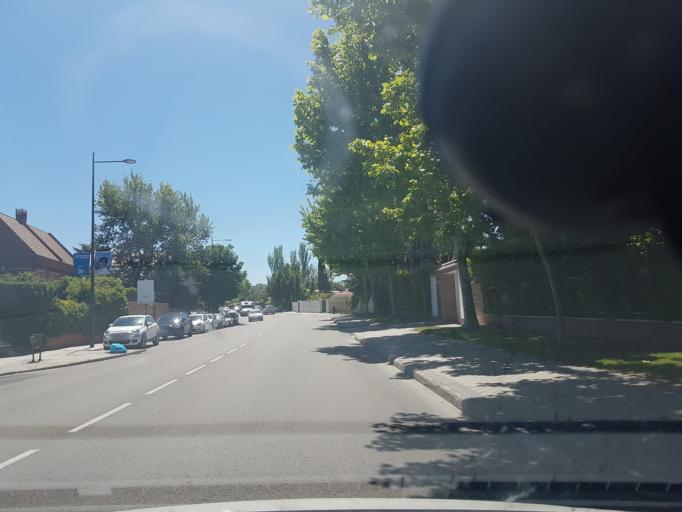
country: ES
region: Madrid
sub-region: Provincia de Madrid
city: Pozuelo de Alarcon
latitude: 40.4384
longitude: -3.8012
